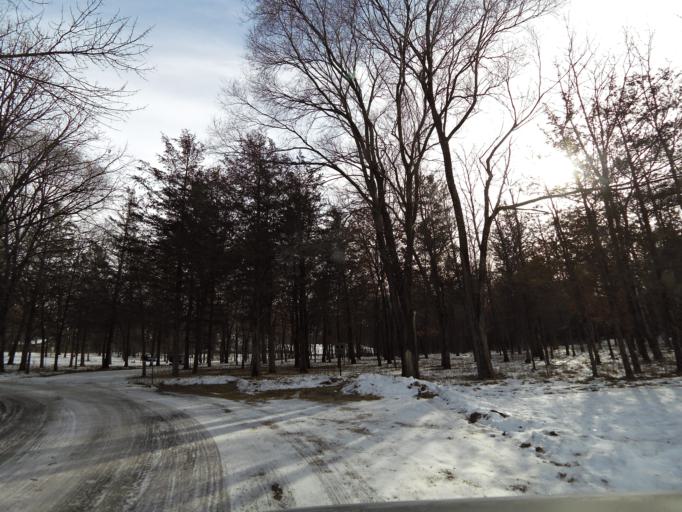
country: US
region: Minnesota
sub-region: Washington County
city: Lake Saint Croix Beach
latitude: 44.9131
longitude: -92.7669
